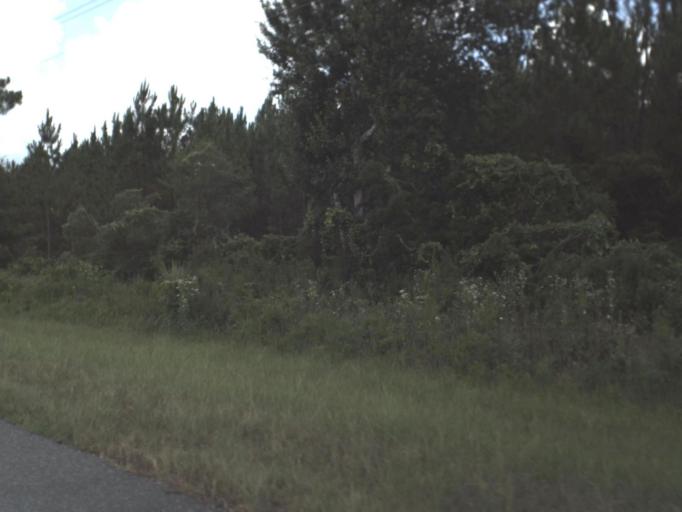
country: US
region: Florida
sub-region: Taylor County
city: Perry
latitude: 30.1428
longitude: -83.8273
